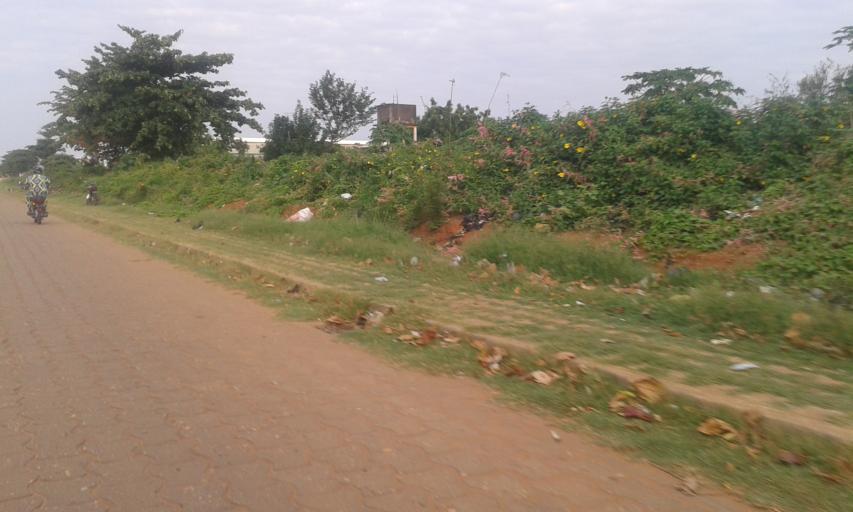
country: BJ
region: Queme
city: Porto-Novo
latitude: 6.4786
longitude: 2.6137
